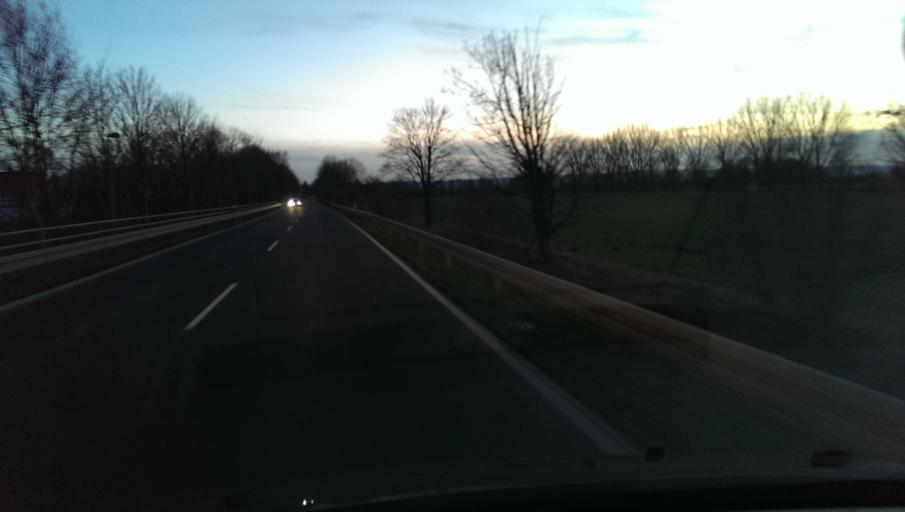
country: DE
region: Saxony-Anhalt
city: Ausleben
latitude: 52.0319
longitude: 11.0938
